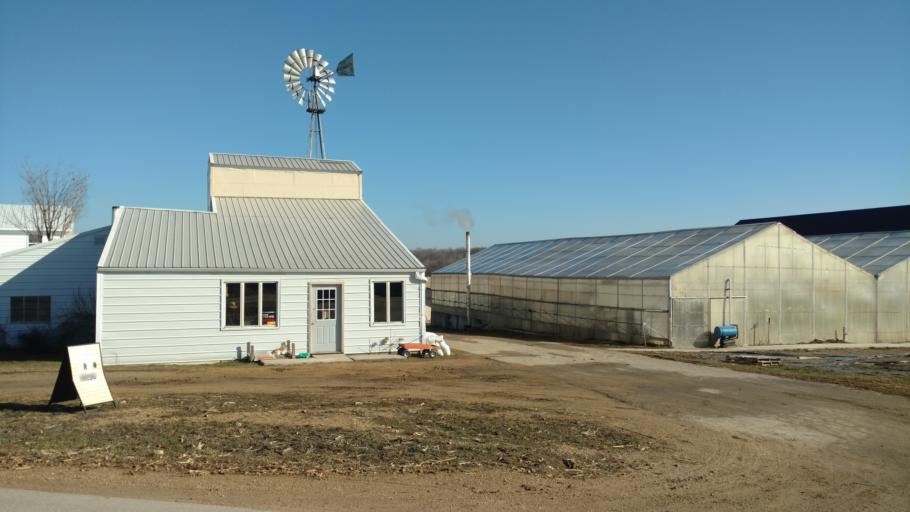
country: US
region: Wisconsin
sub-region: Vernon County
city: Hillsboro
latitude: 43.6141
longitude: -90.4445
